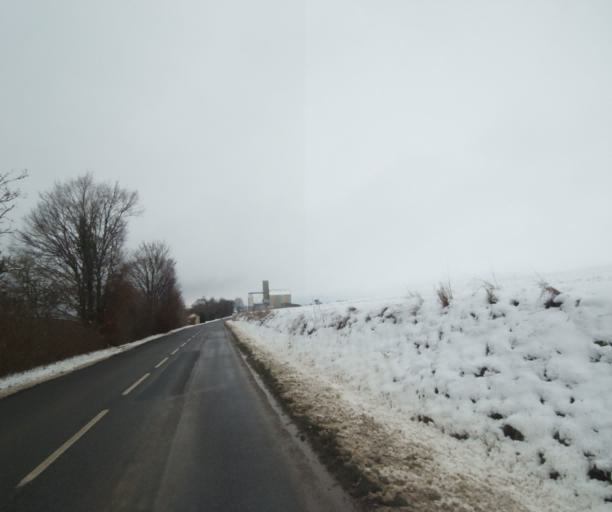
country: FR
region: Champagne-Ardenne
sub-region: Departement de la Haute-Marne
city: Wassy
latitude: 48.4303
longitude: 4.9625
